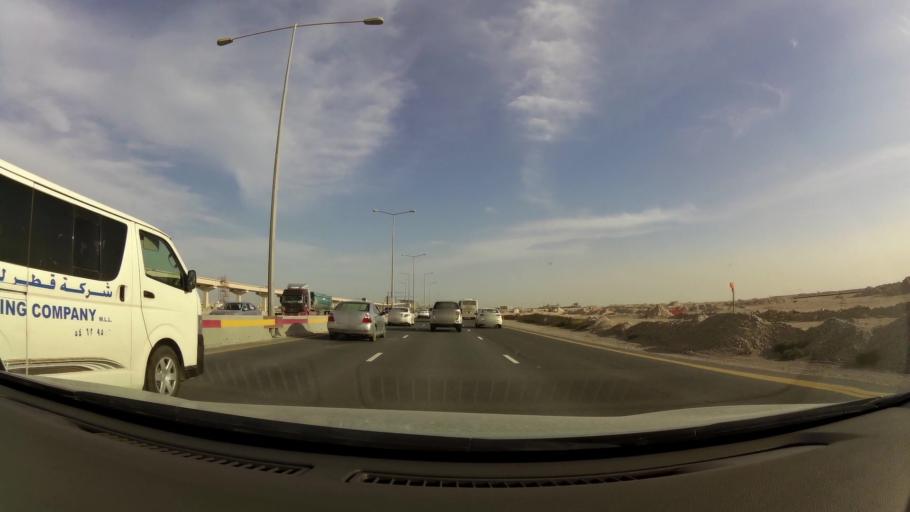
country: QA
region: Al Wakrah
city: Al Wakrah
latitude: 25.2024
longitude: 51.5903
